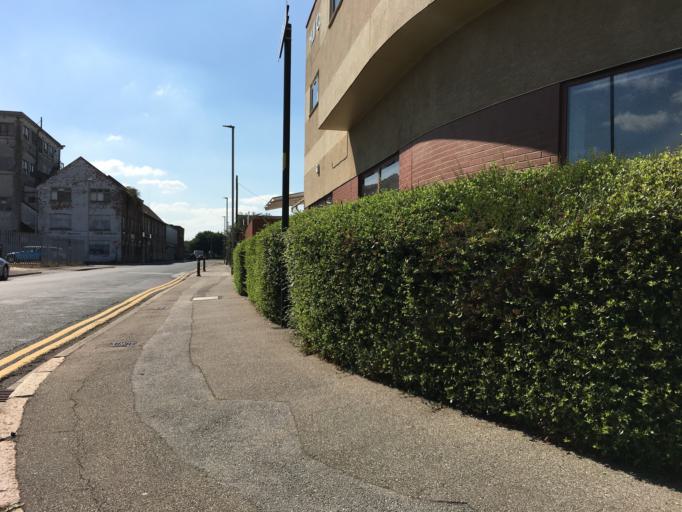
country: GB
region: England
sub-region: City of Kingston upon Hull
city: Hull
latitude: 53.7515
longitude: -0.3366
